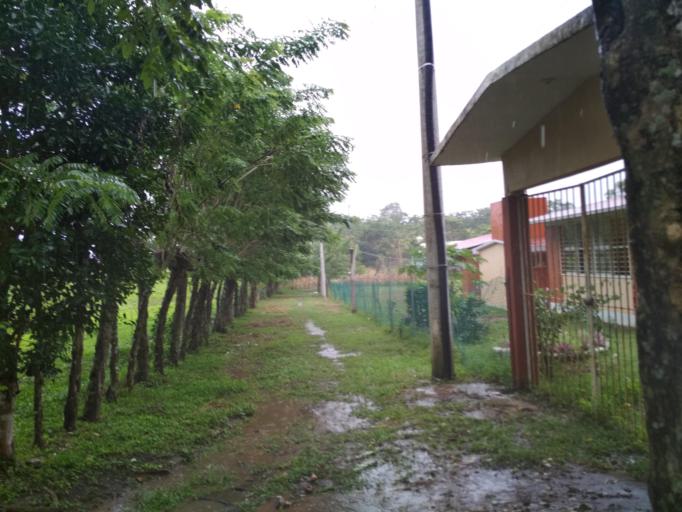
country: MX
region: Veracruz
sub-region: San Andres Tuxtla
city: Soyata
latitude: 18.4141
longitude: -95.3073
